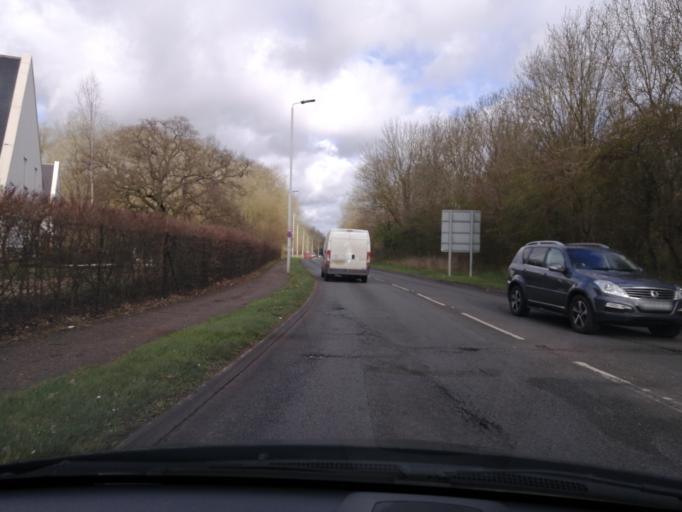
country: GB
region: England
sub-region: Peterborough
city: Marholm
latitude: 52.5923
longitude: -0.2870
